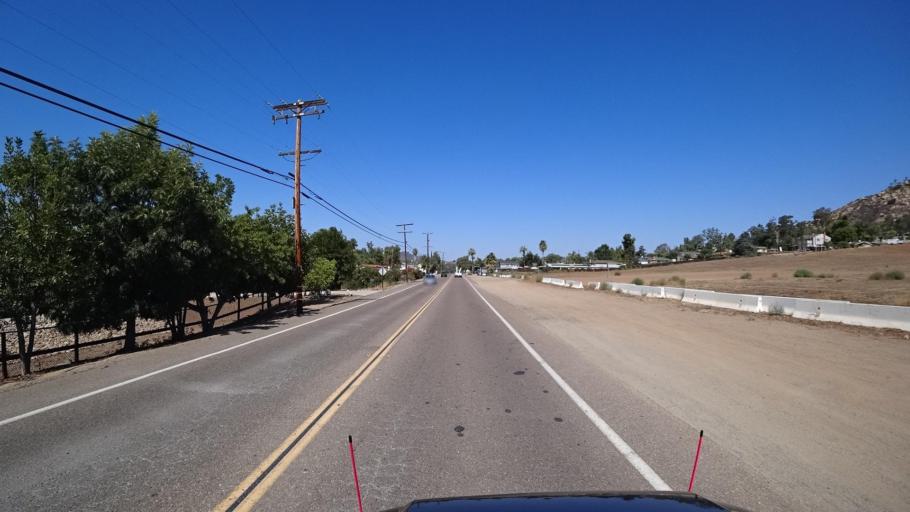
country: US
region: California
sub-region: San Diego County
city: Granite Hills
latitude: 32.8029
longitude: -116.9063
